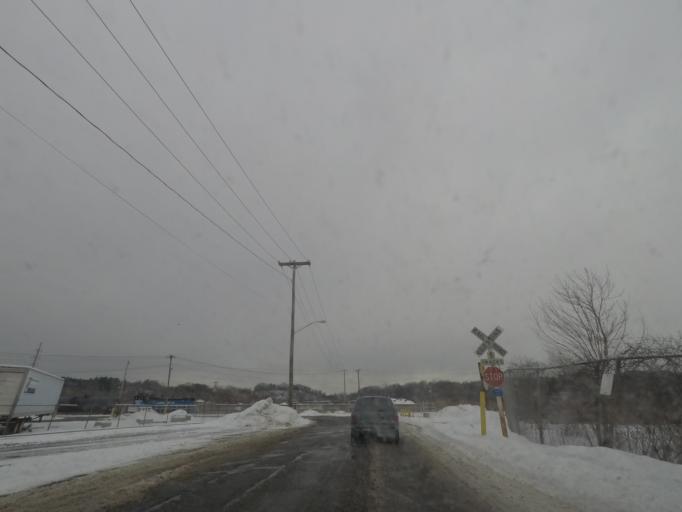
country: US
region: New York
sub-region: Rensselaer County
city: Rensselaer
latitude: 42.6226
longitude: -73.7631
